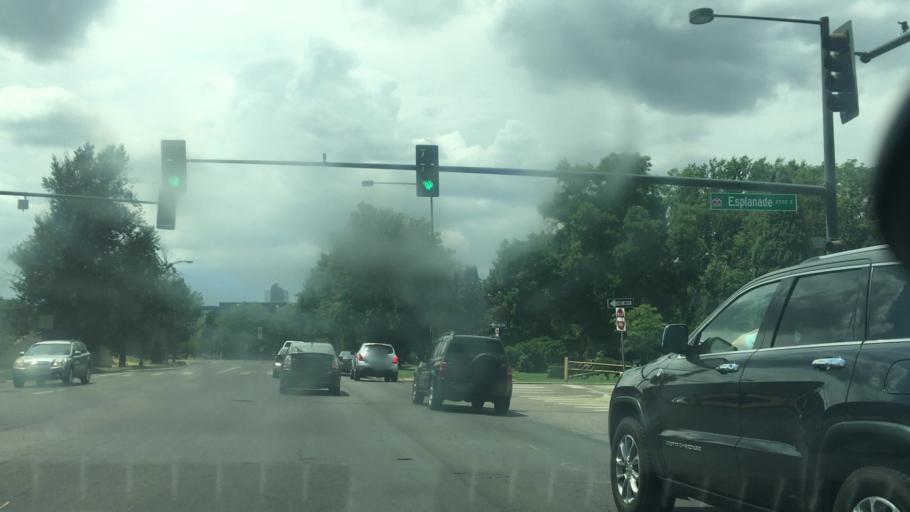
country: US
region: Colorado
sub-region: Denver County
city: Denver
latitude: 39.7439
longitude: -104.9566
